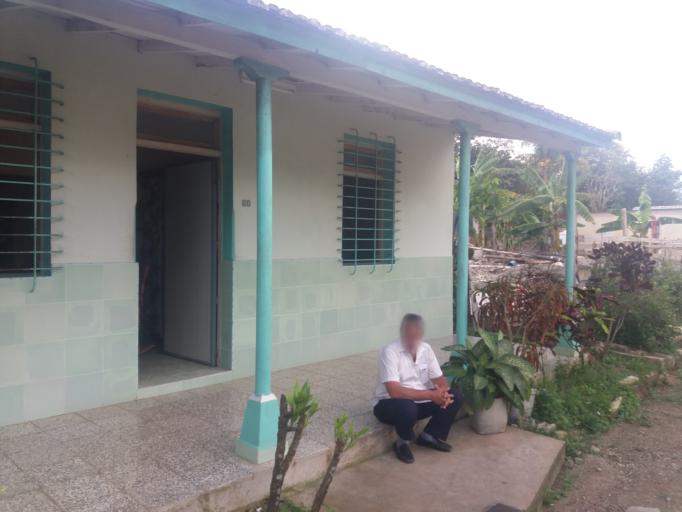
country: CU
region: Cienfuegos
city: Rodas
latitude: 22.3523
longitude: -80.5114
